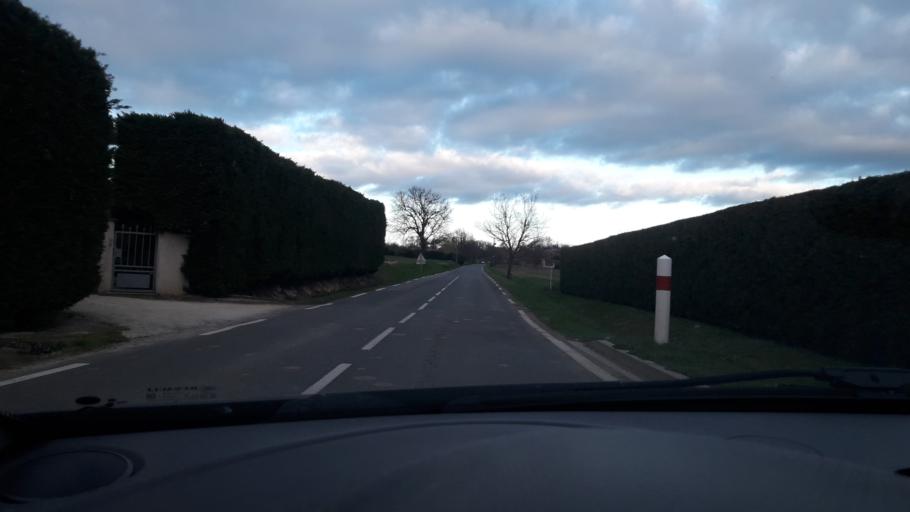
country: FR
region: Midi-Pyrenees
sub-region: Departement de la Haute-Garonne
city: Launac
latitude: 43.7332
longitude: 1.1043
